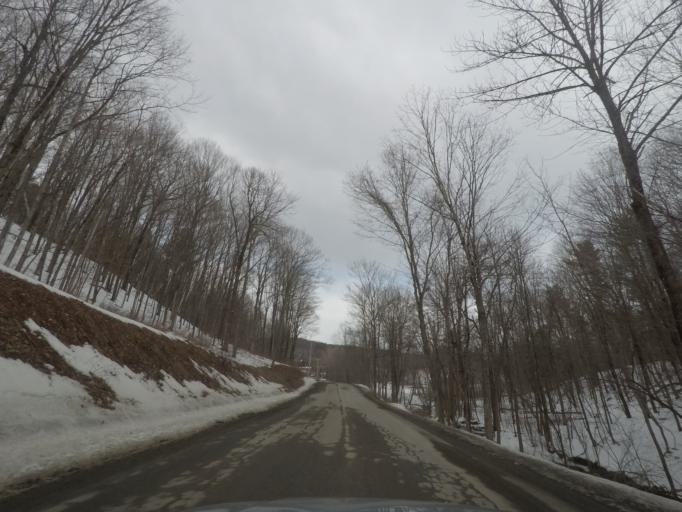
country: US
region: New York
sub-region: Saratoga County
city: Waterford
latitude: 42.7784
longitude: -73.6116
